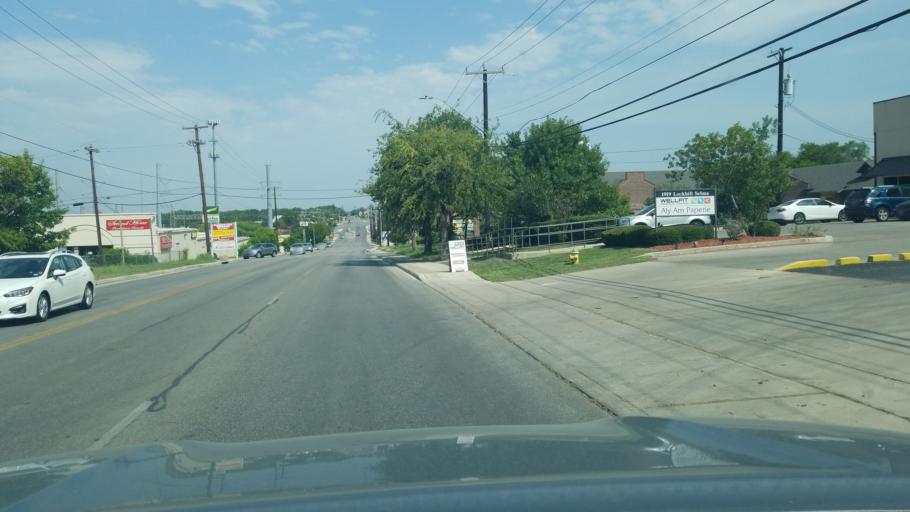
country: US
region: Texas
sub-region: Bexar County
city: Castle Hills
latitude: 29.5374
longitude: -98.5233
